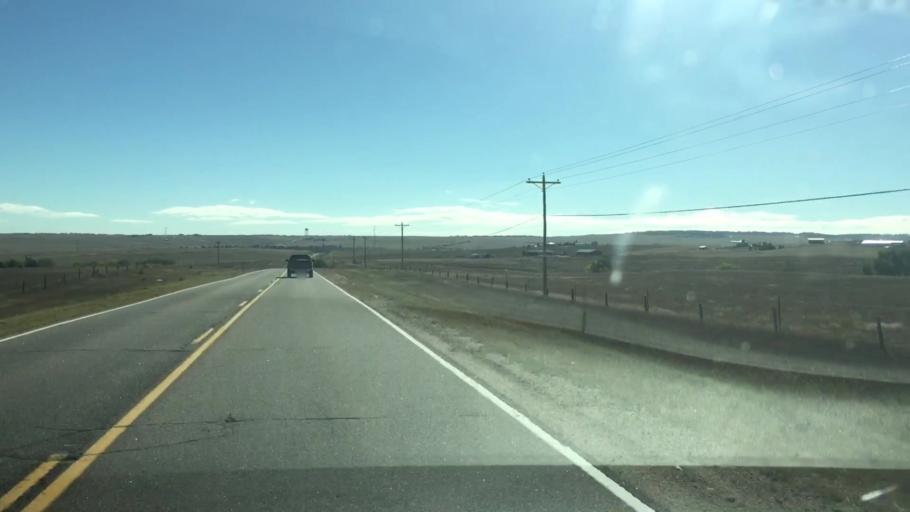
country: US
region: Colorado
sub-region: Elbert County
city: Kiowa
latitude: 39.3527
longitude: -104.4993
